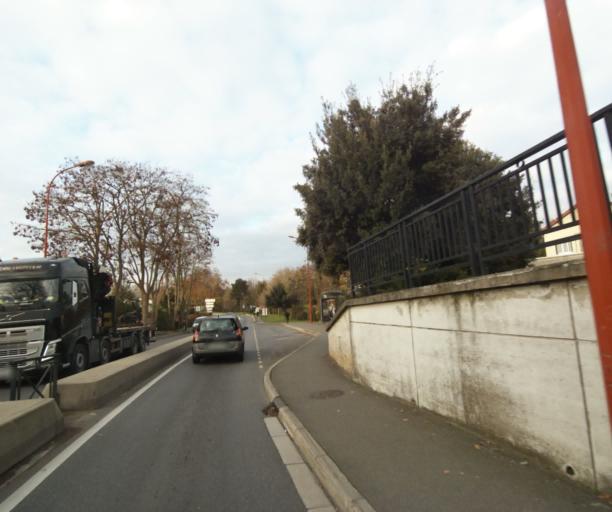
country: FR
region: Ile-de-France
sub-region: Departement du Val-d'Oise
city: Gonesse
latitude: 48.9866
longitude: 2.4372
